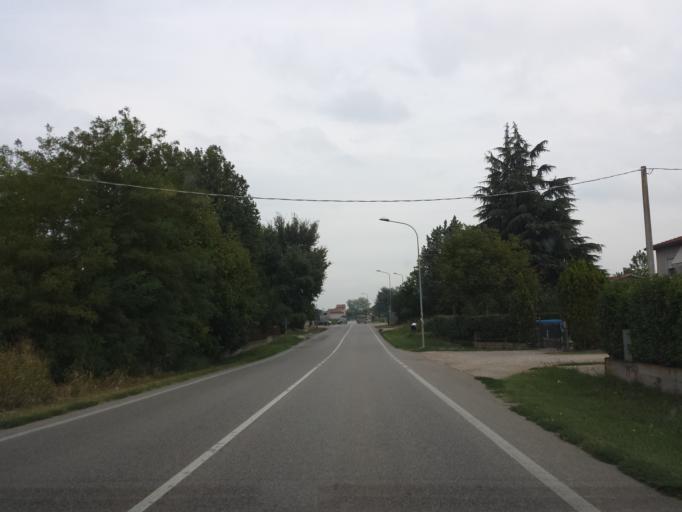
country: IT
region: Veneto
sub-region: Provincia di Verona
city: San Gregorio
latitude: 45.3362
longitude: 11.2864
